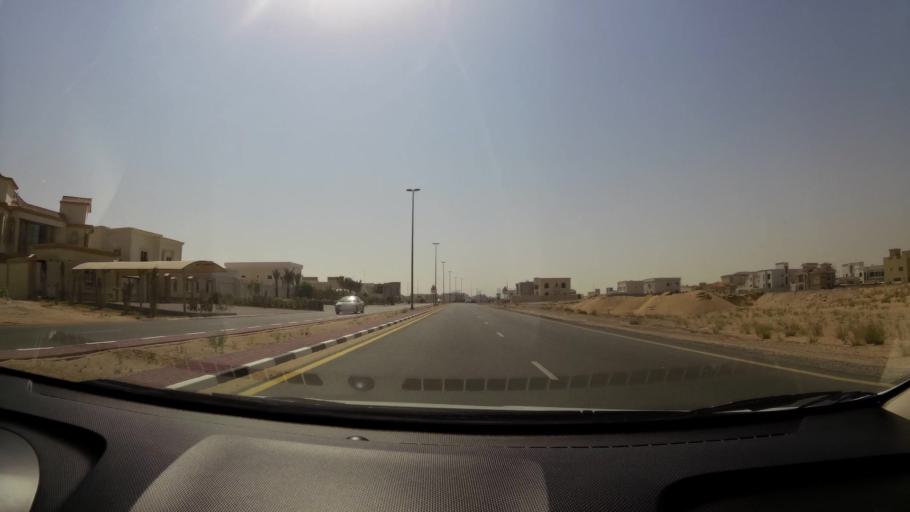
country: AE
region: Ajman
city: Ajman
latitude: 25.4054
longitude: 55.5361
